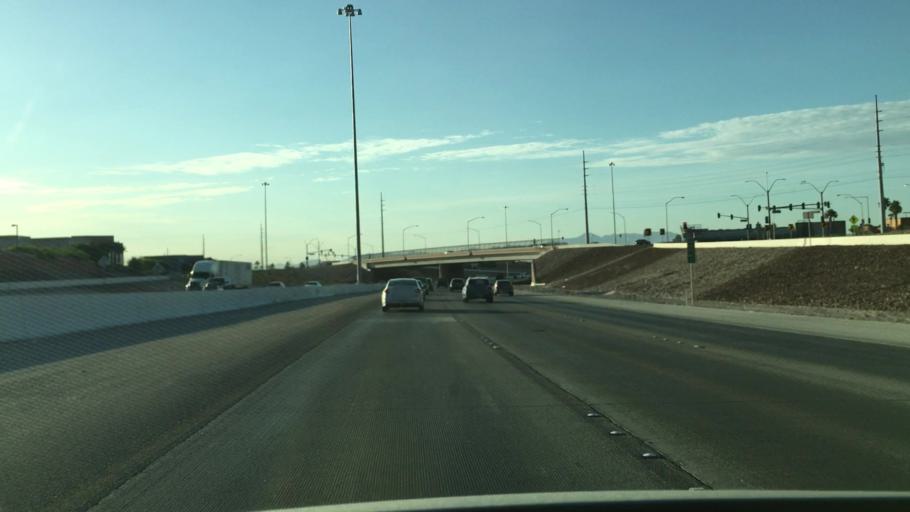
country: US
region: Nevada
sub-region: Clark County
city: Summerlin South
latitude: 36.1166
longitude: -115.3053
